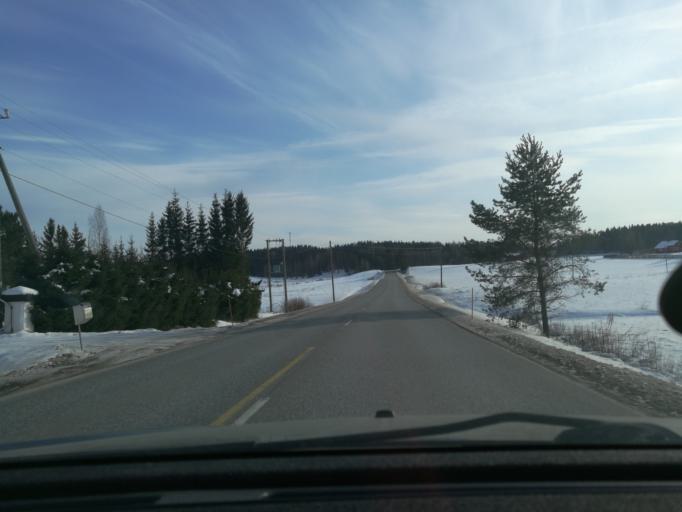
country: FI
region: Uusimaa
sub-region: Helsinki
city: Saukkola
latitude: 60.3940
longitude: 24.0738
